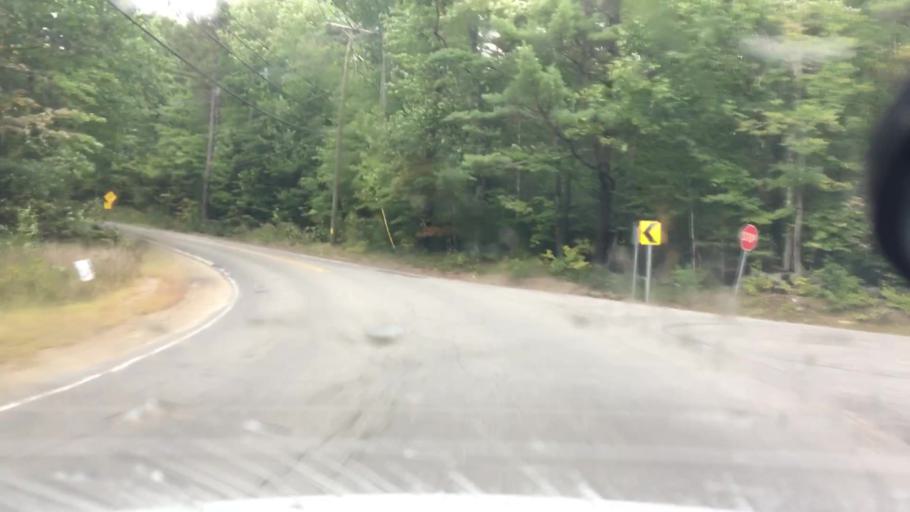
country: US
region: New Hampshire
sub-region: Carroll County
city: Wakefield
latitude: 43.5813
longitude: -71.0151
